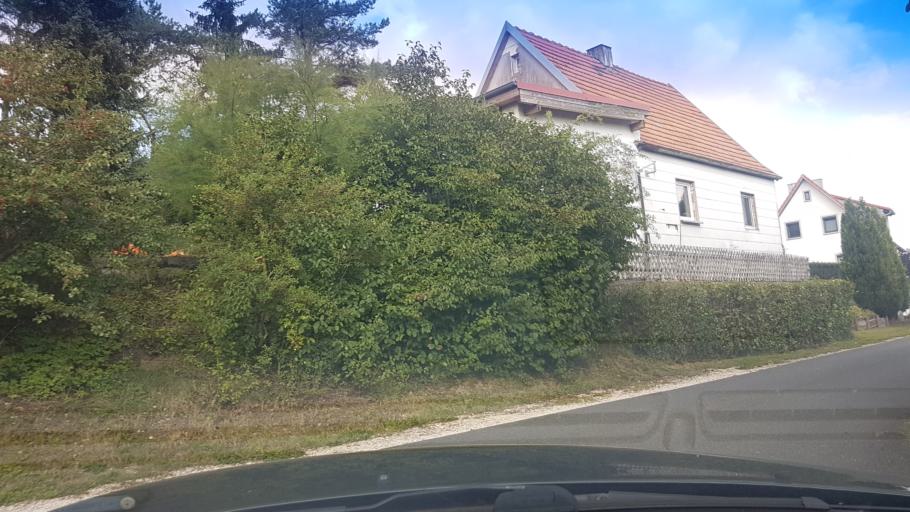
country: DE
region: Bavaria
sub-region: Upper Franconia
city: Konigsfeld
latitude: 49.9455
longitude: 11.1595
